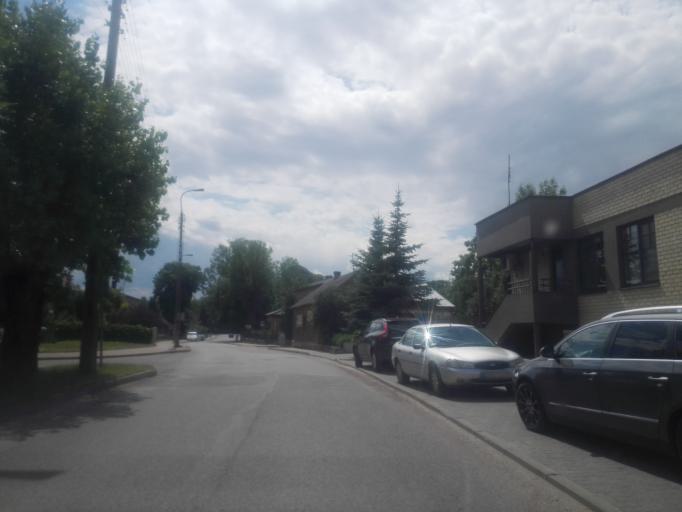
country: PL
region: Podlasie
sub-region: Powiat sejnenski
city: Sejny
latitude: 54.1104
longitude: 23.3492
